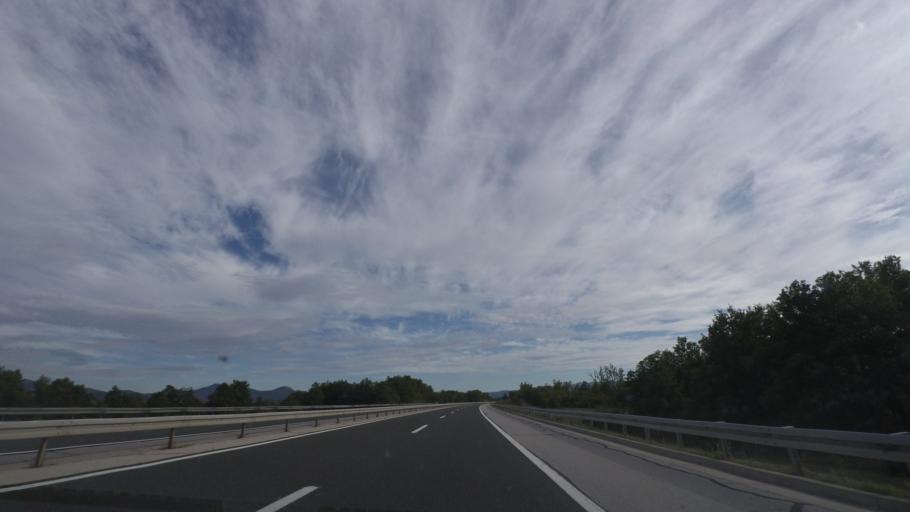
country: HR
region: Zadarska
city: Obrovac
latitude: 44.4267
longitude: 15.6333
